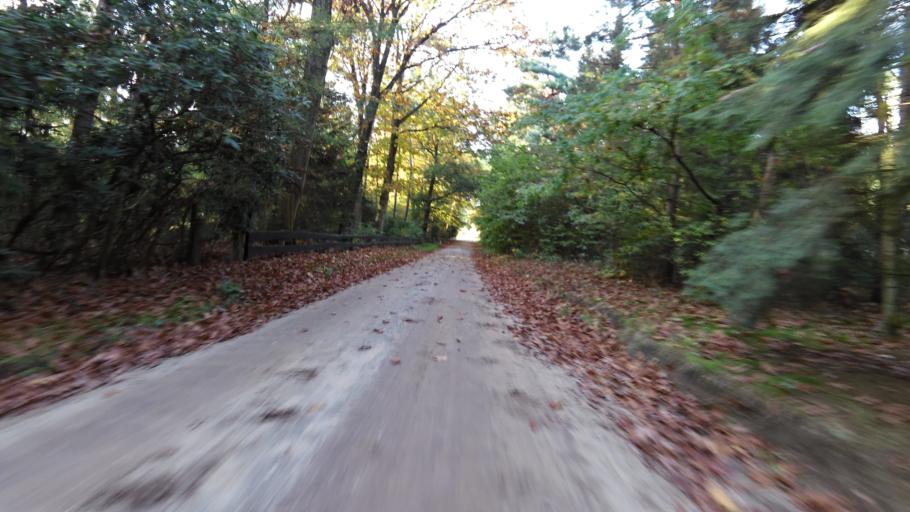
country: NL
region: Gelderland
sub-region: Gemeente Ede
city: Lunteren
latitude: 52.0784
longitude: 5.6602
